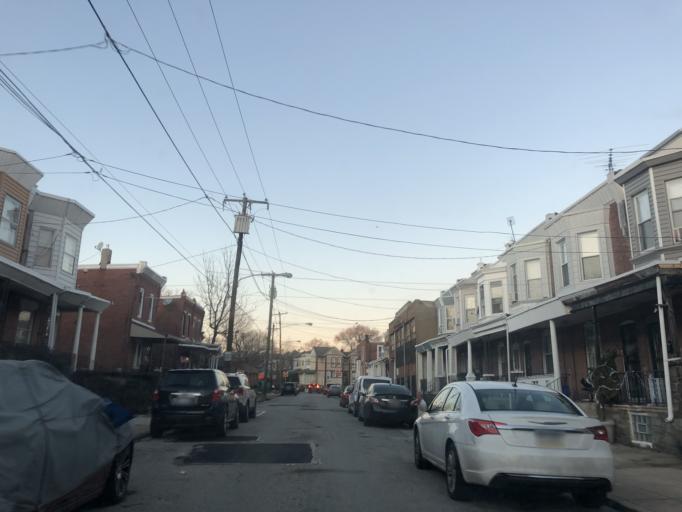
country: US
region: Pennsylvania
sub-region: Delaware County
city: Millbourne
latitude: 39.9710
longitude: -75.2461
